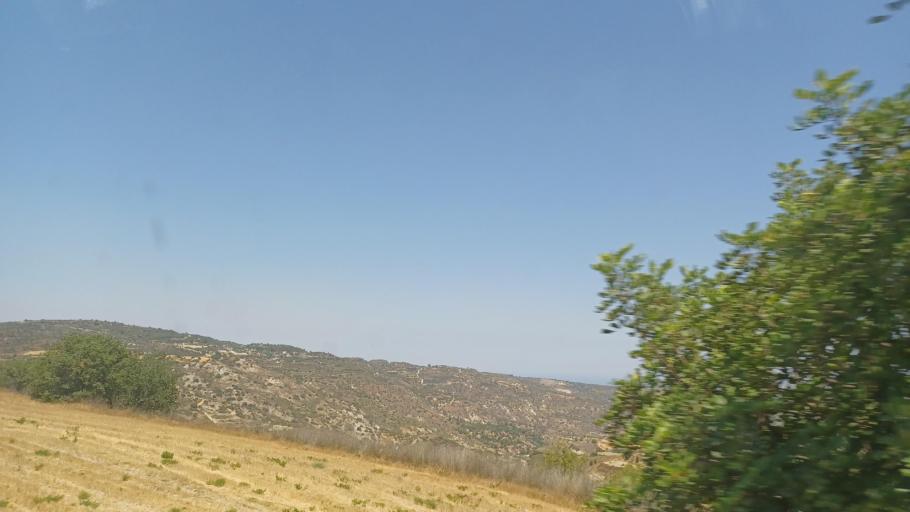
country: CY
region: Pafos
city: Tala
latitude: 34.8959
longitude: 32.4639
